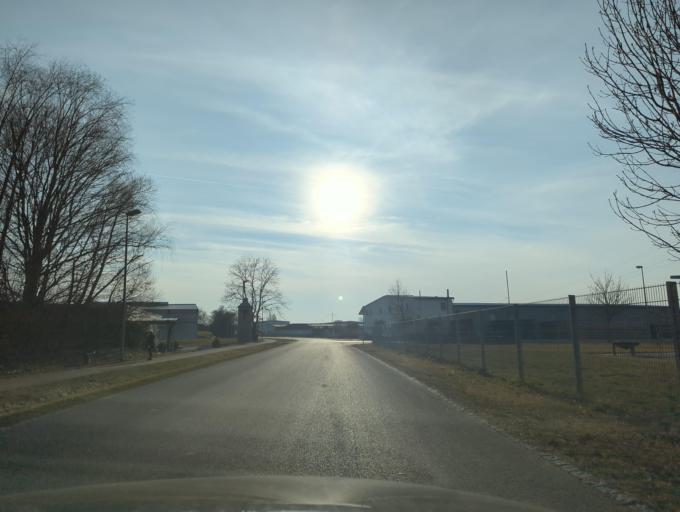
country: DE
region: Bavaria
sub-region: Swabia
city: Leipheim
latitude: 48.4603
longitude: 10.2146
